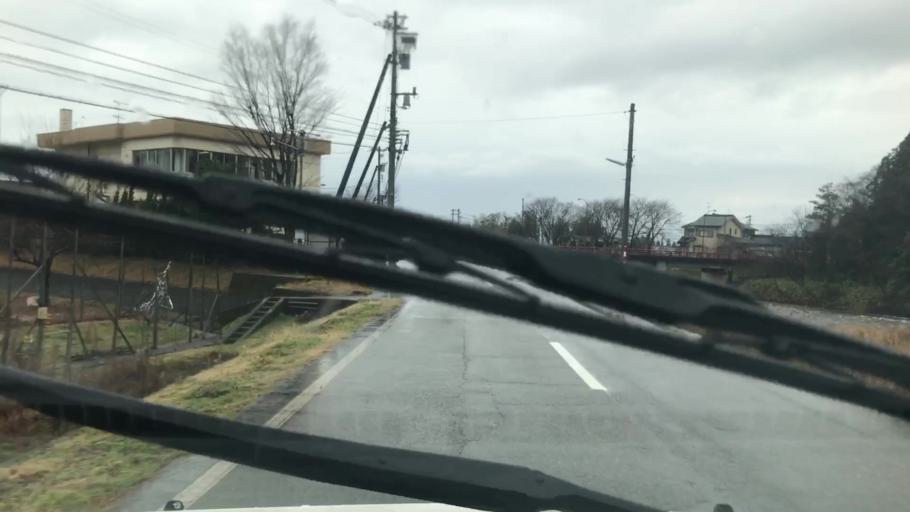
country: JP
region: Toyama
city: Toyama-shi
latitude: 36.6056
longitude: 137.2911
